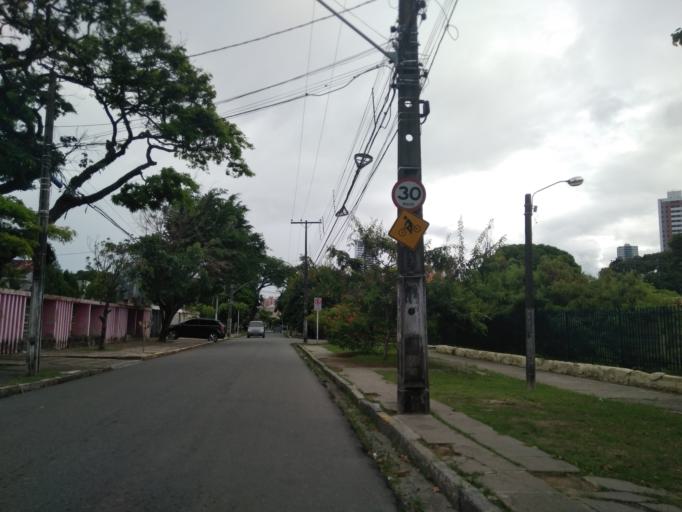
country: BR
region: Pernambuco
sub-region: Recife
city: Recife
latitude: -8.0333
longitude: -34.8874
